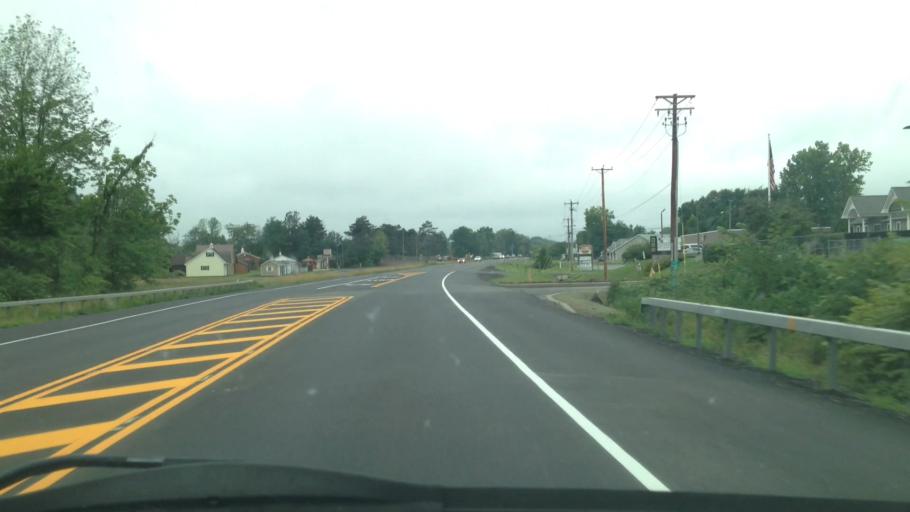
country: US
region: New York
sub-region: Ulster County
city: Clintondale
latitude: 41.7373
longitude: -74.0292
